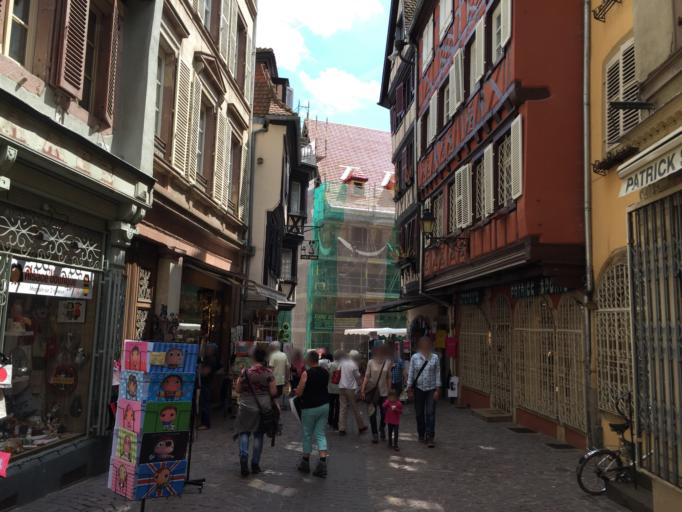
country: FR
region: Alsace
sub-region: Departement du Haut-Rhin
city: Colmar
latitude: 48.0764
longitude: 7.3584
